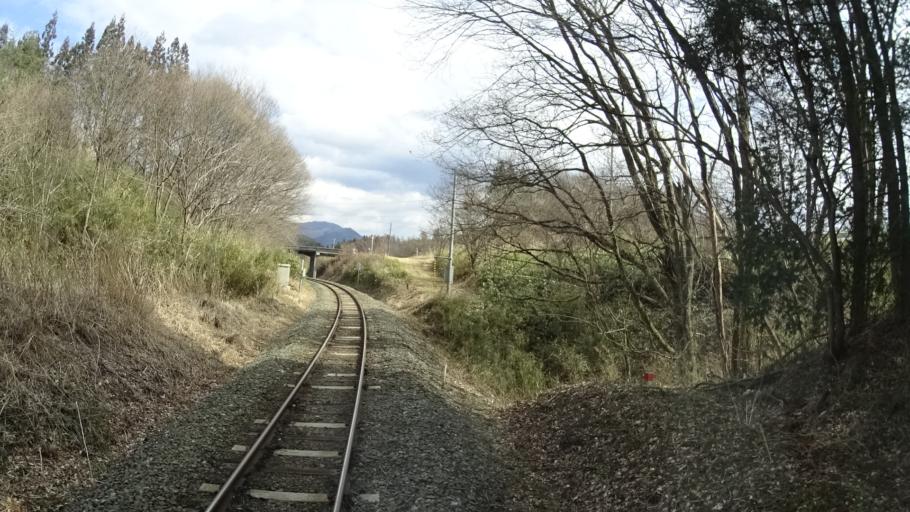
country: JP
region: Iwate
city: Tono
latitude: 39.3524
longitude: 141.3331
